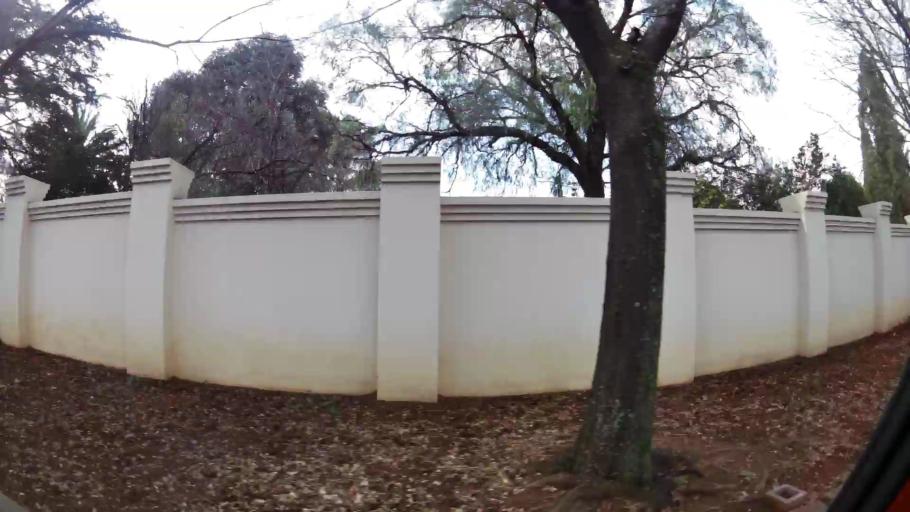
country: ZA
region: Gauteng
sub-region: Sedibeng District Municipality
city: Vanderbijlpark
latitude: -26.7428
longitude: 27.8338
